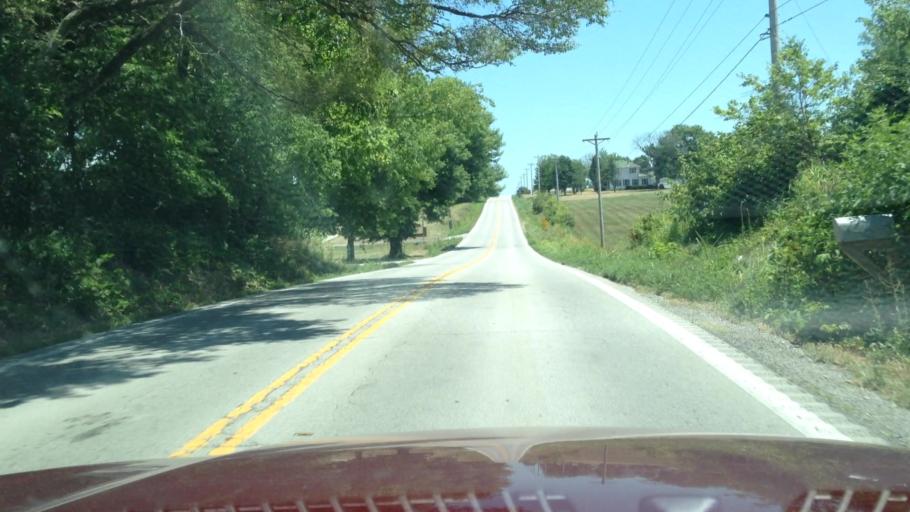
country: US
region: Missouri
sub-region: Clay County
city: Kearney
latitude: 39.3679
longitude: -94.4543
